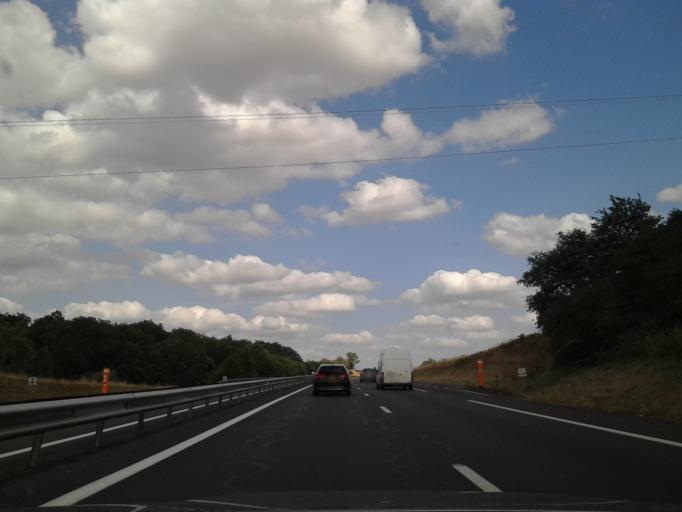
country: FR
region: Auvergne
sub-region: Departement de l'Allier
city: Doyet
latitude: 46.3487
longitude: 2.8526
